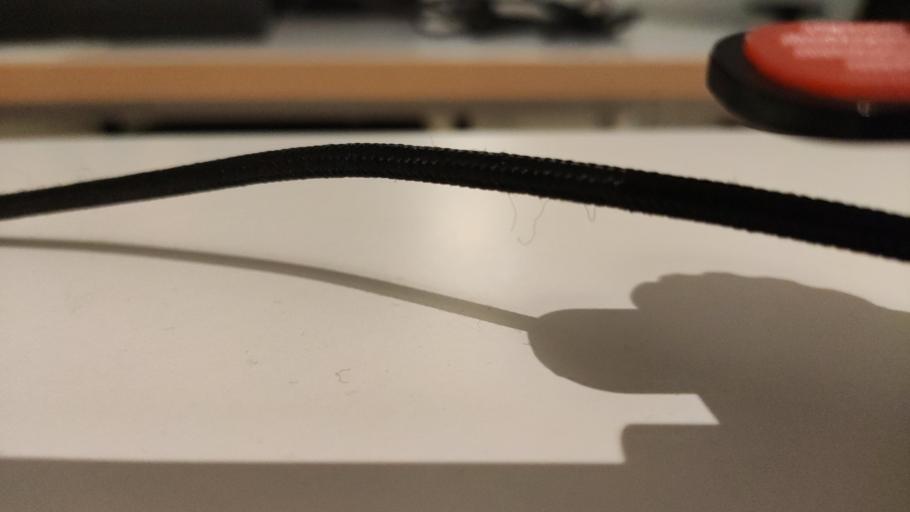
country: RU
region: Moskovskaya
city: Rogachevo
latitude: 56.4114
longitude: 37.2259
